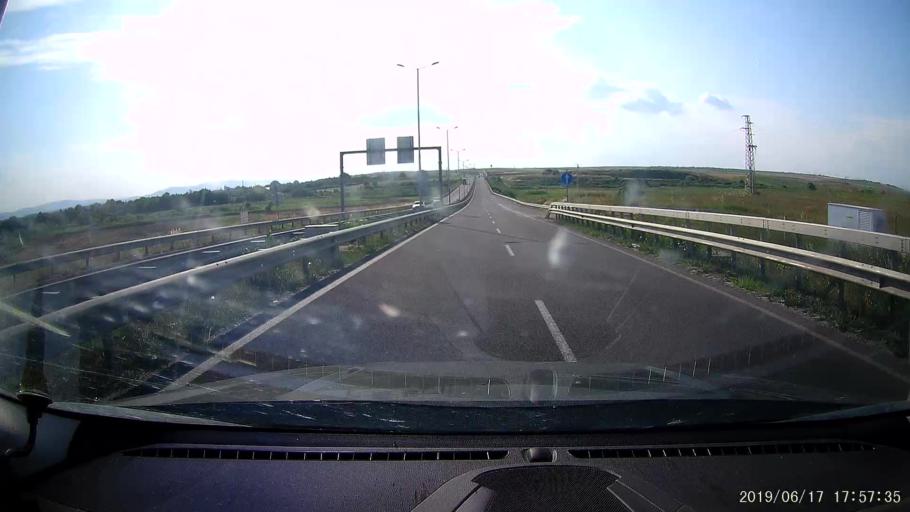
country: GR
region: East Macedonia and Thrace
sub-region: Nomos Evrou
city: Rizia
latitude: 41.7220
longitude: 26.3333
